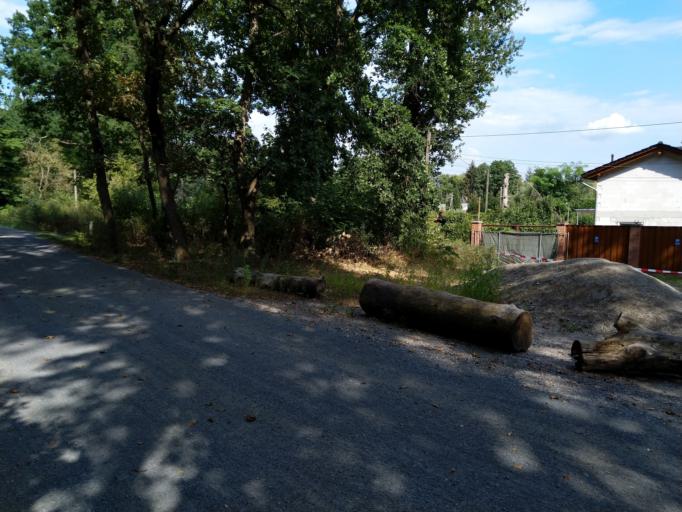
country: DE
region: Berlin
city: Friedrichshagen
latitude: 52.4659
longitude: 13.6200
